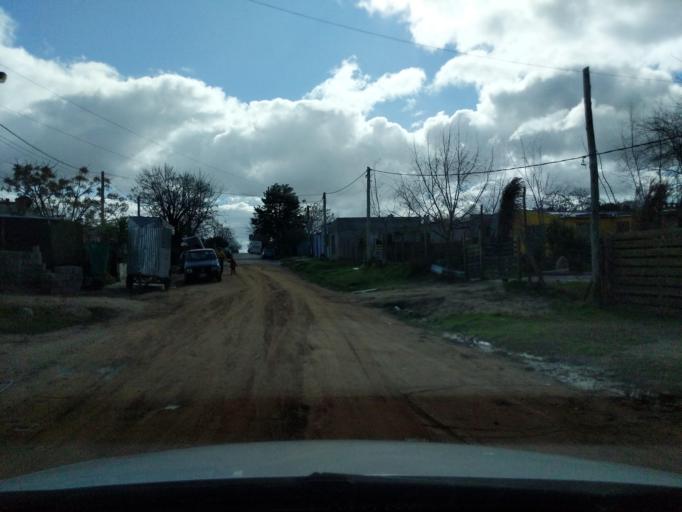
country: UY
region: Florida
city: Florida
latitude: -34.0956
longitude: -56.2063
